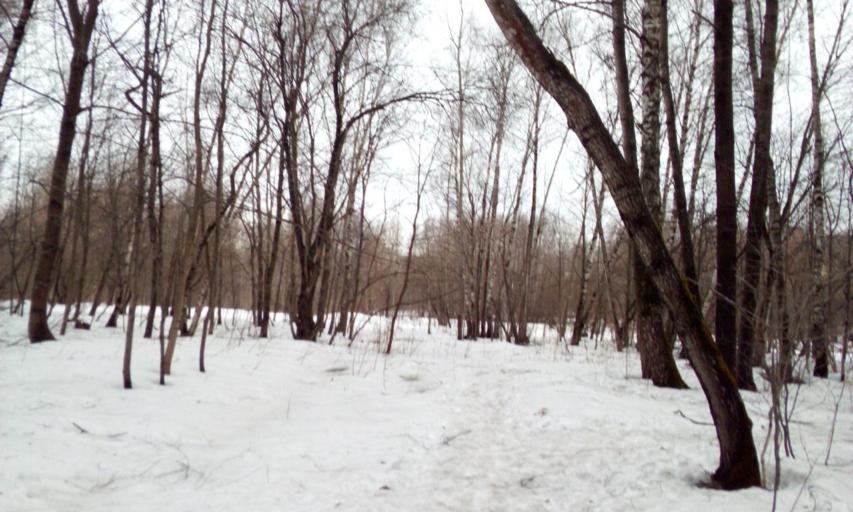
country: RU
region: Moskovskaya
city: Vostryakovo
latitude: 55.6539
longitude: 37.4553
